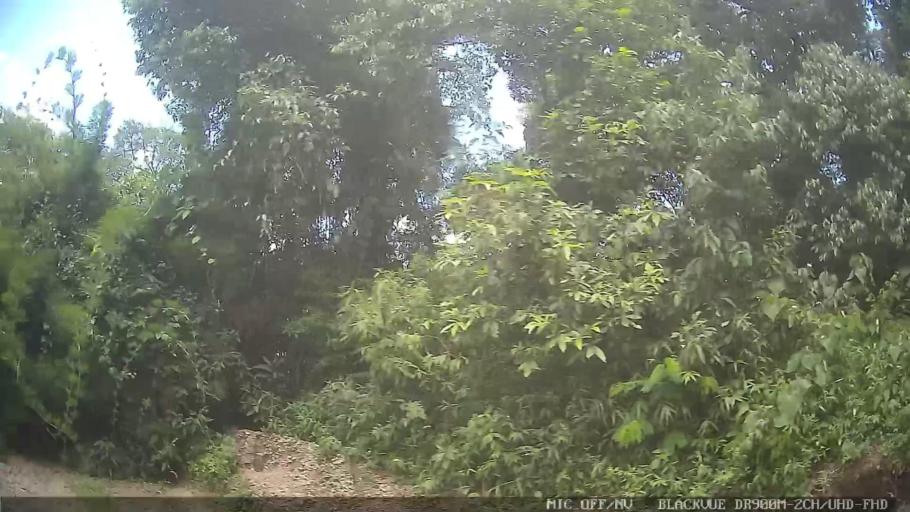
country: BR
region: Minas Gerais
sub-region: Extrema
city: Extrema
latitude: -22.8902
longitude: -46.3221
